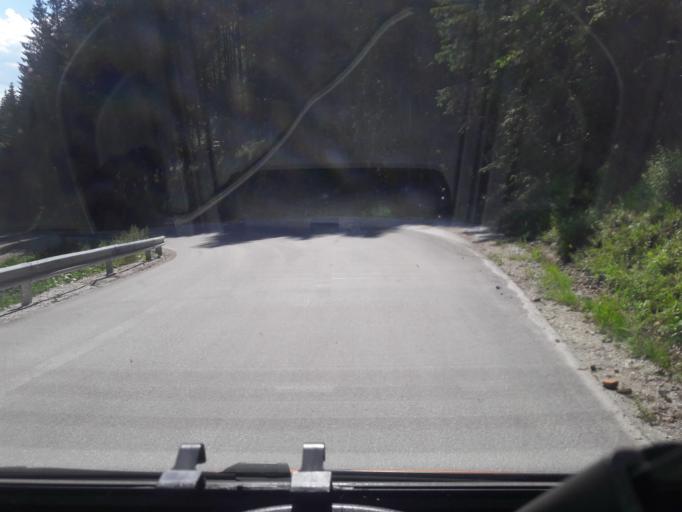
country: AT
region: Styria
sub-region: Politischer Bezirk Liezen
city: Tauplitz
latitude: 47.5708
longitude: 13.9599
